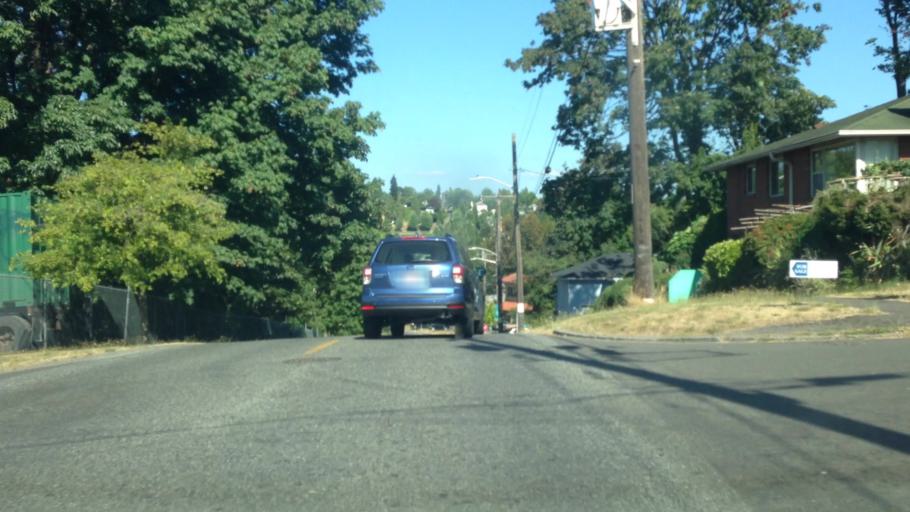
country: US
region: Washington
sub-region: King County
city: Seattle
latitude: 47.5829
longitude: -122.3044
